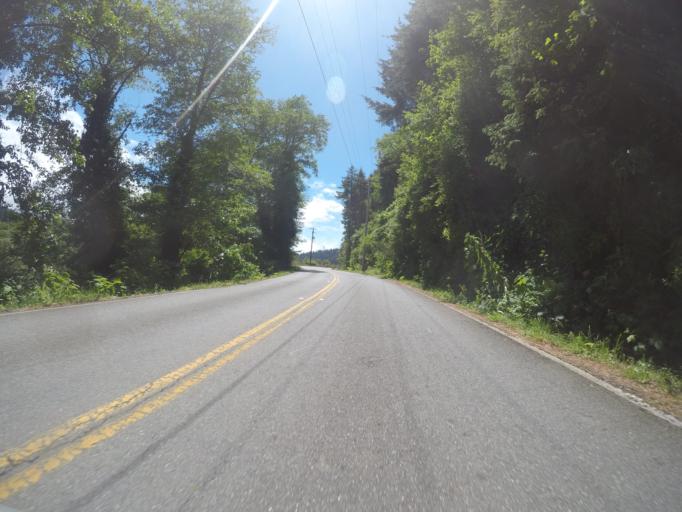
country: US
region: California
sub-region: Del Norte County
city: Bertsch-Oceanview
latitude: 41.5491
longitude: -124.0608
